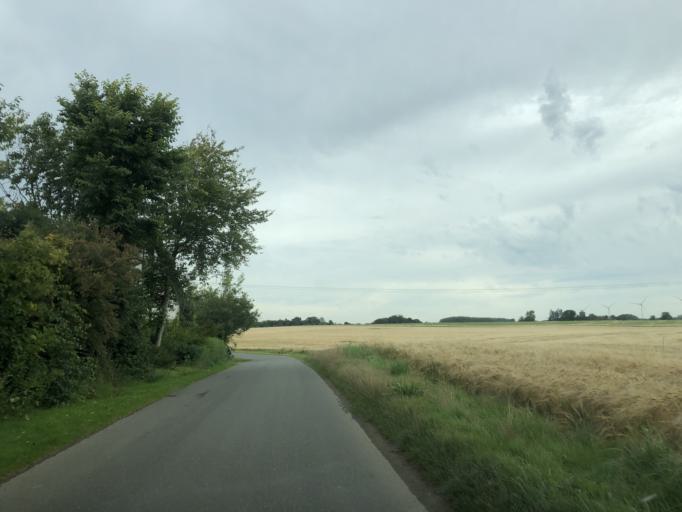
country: DK
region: Central Jutland
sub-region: Holstebro Kommune
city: Holstebro
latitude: 56.3994
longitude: 8.5916
